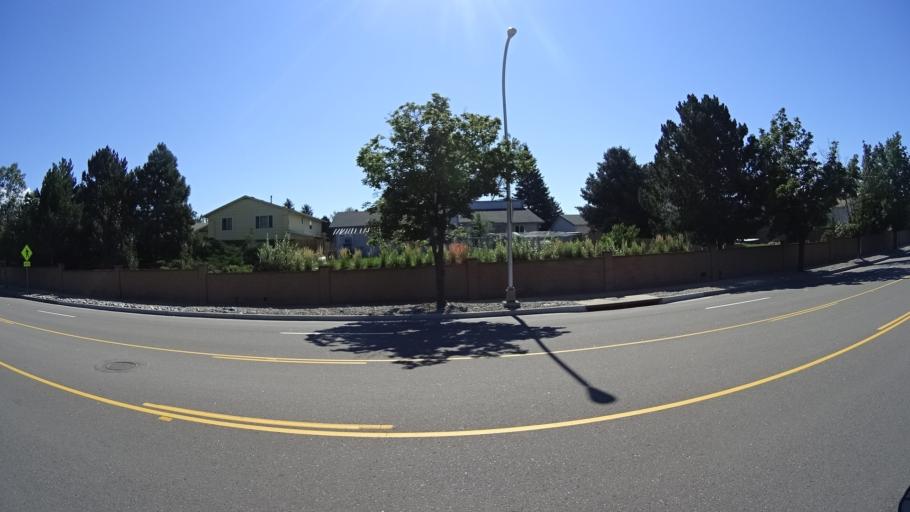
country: US
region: Colorado
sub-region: El Paso County
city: Black Forest
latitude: 38.9533
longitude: -104.7714
